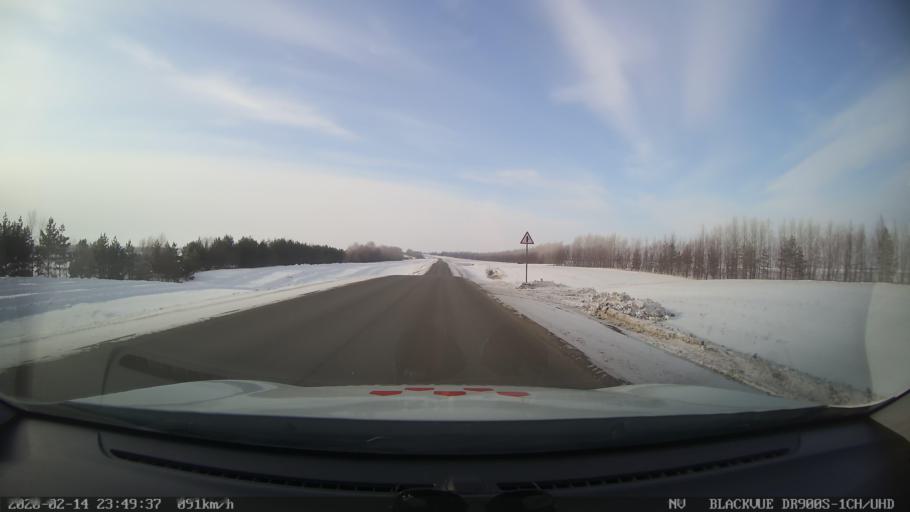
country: RU
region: Tatarstan
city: Kuybyshevskiy Zaton
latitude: 55.2549
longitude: 49.1780
